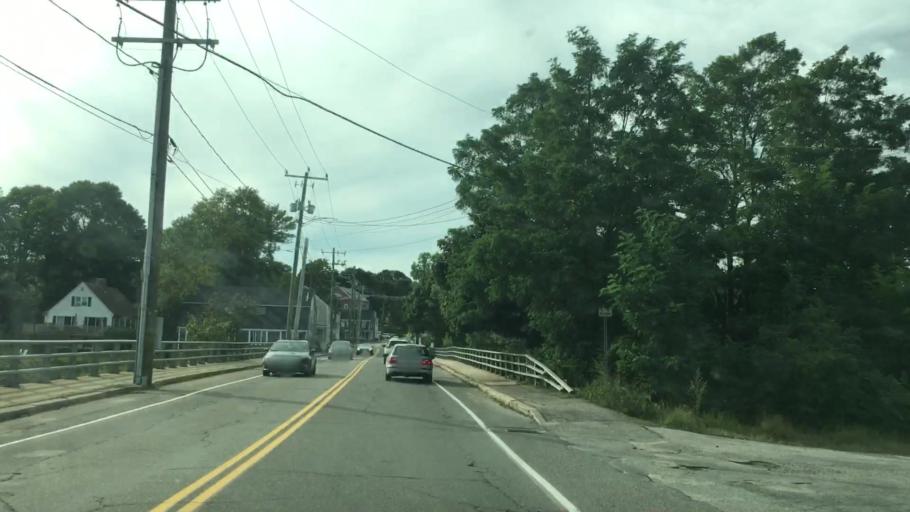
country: US
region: New Hampshire
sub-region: Rockingham County
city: Portsmouth
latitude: 43.0796
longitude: -70.7646
